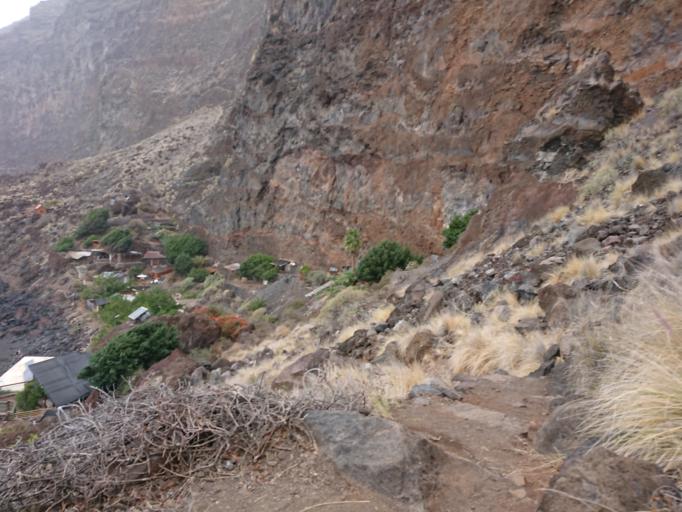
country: ES
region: Canary Islands
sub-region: Provincia de Santa Cruz de Tenerife
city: Tijarafe
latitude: 28.7210
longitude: -17.9792
